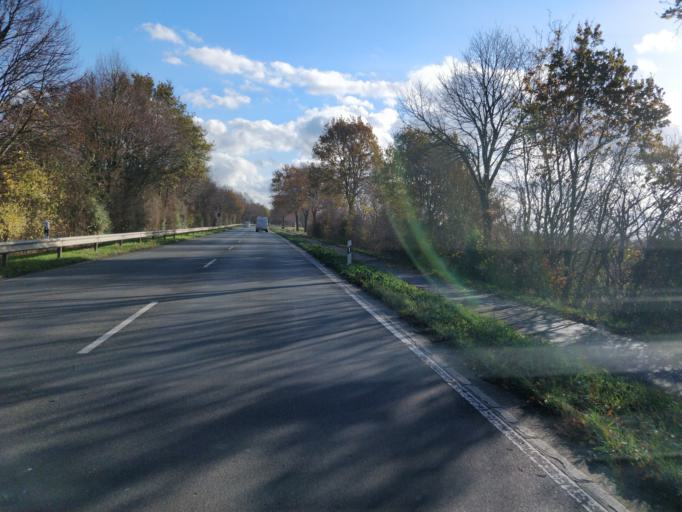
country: DE
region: North Rhine-Westphalia
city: Rees
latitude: 51.7839
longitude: 6.3751
